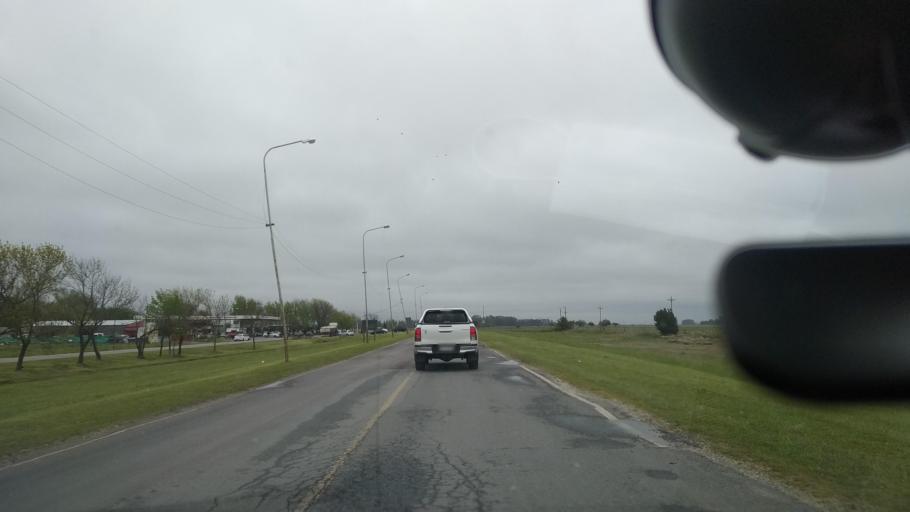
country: AR
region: Buenos Aires
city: Veronica
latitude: -35.5278
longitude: -57.3251
